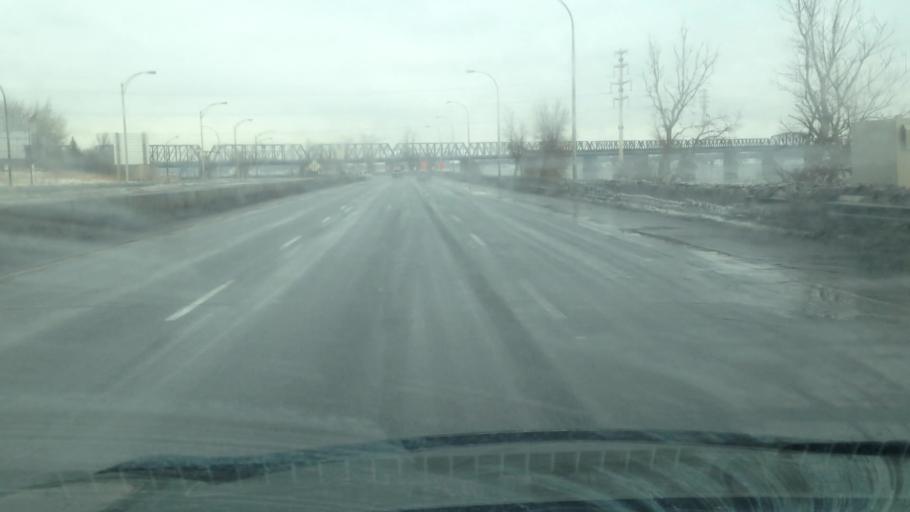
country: CA
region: Quebec
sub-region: Monteregie
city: Longueuil
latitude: 45.4831
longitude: -73.5384
